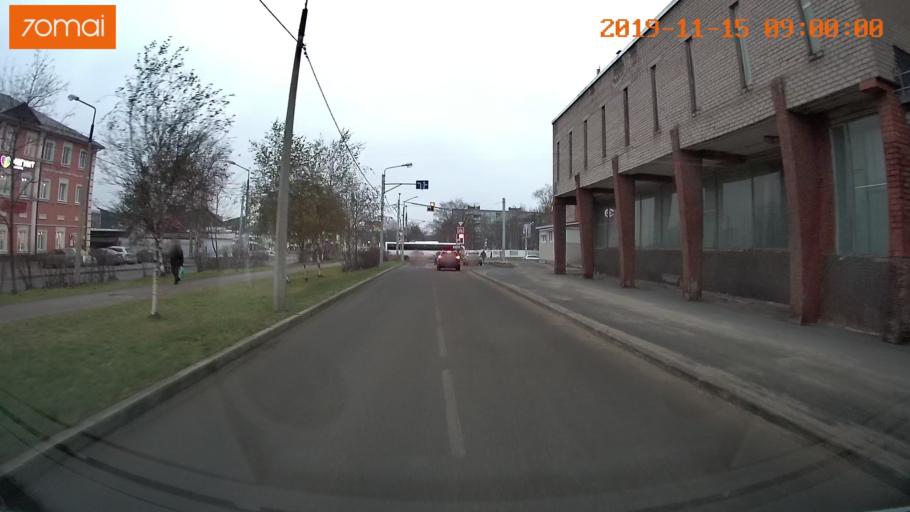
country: RU
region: Vologda
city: Cherepovets
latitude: 59.1295
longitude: 37.9246
